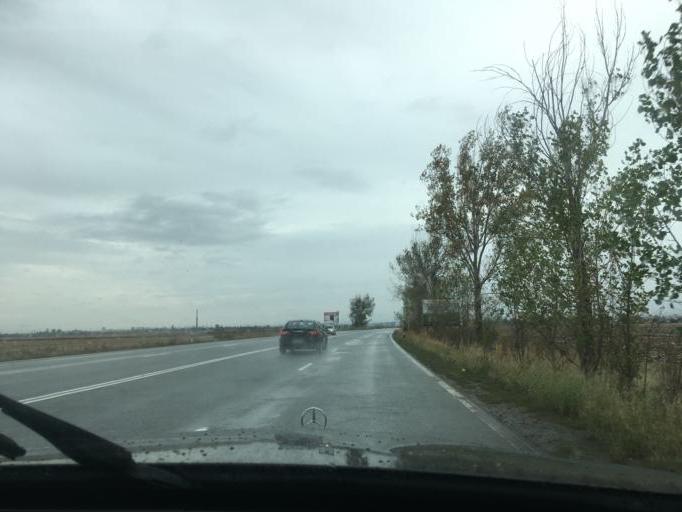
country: BG
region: Sofiya
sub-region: Obshtina Bozhurishte
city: Bozhurishte
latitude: 42.7644
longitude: 23.2151
